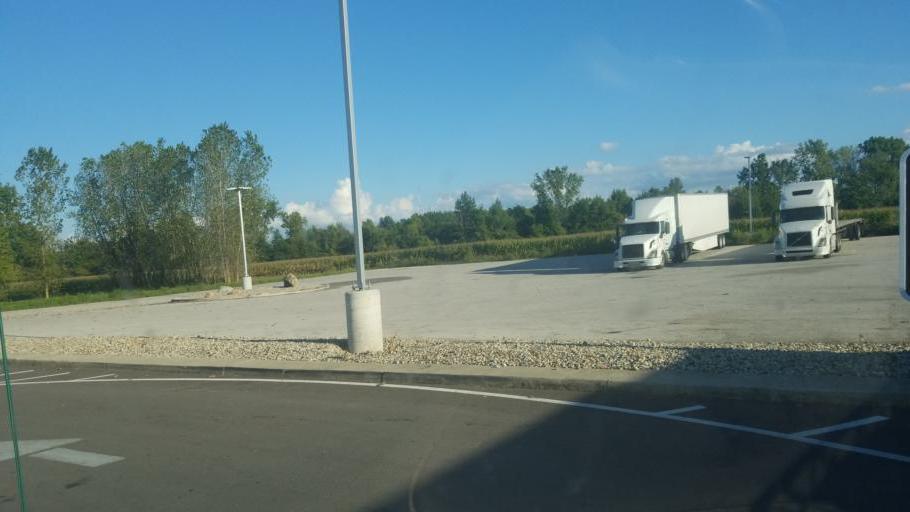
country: US
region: Ohio
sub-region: Wyandot County
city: Carey
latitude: 40.9418
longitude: -83.3952
